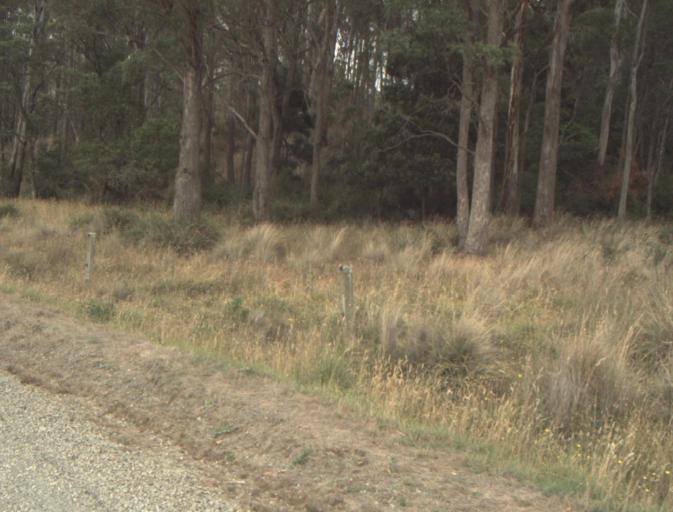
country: AU
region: Tasmania
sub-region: Northern Midlands
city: Evandale
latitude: -41.4816
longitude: 147.4420
